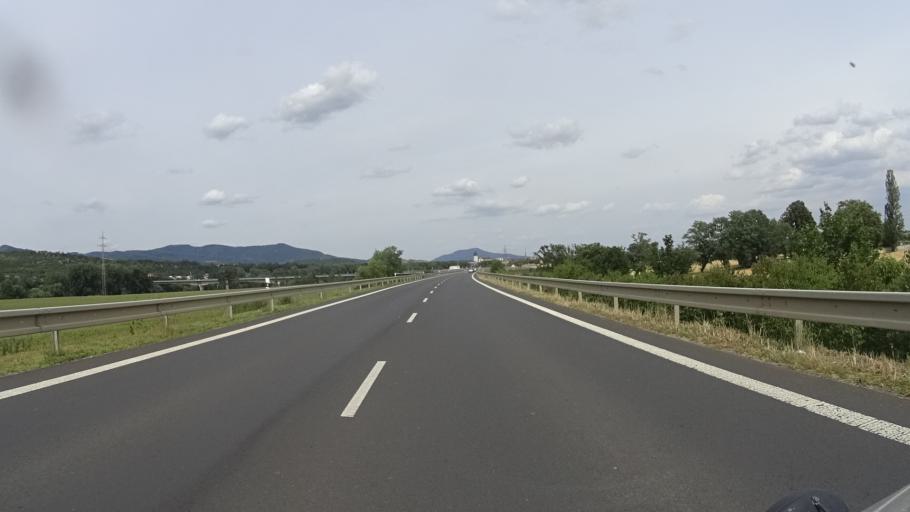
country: CZ
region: Ustecky
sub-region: Okres Litomerice
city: Litomerice
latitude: 50.5223
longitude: 14.1060
